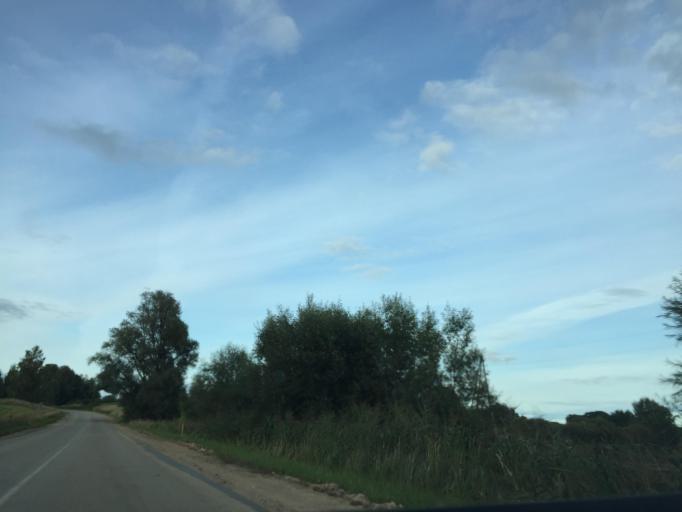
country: LV
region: Viesite
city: Viesite
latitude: 56.3024
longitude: 25.4394
